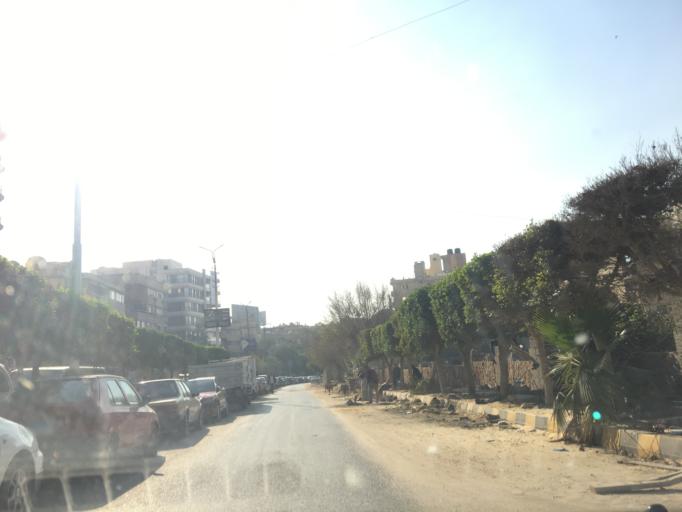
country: EG
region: Muhafazat al Qahirah
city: Cairo
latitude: 30.0864
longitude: 31.3313
